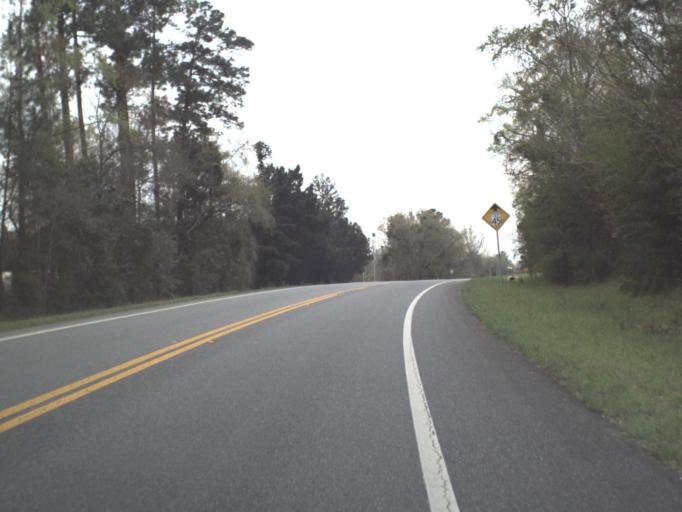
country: US
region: Florida
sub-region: Calhoun County
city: Blountstown
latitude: 30.4416
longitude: -85.1832
